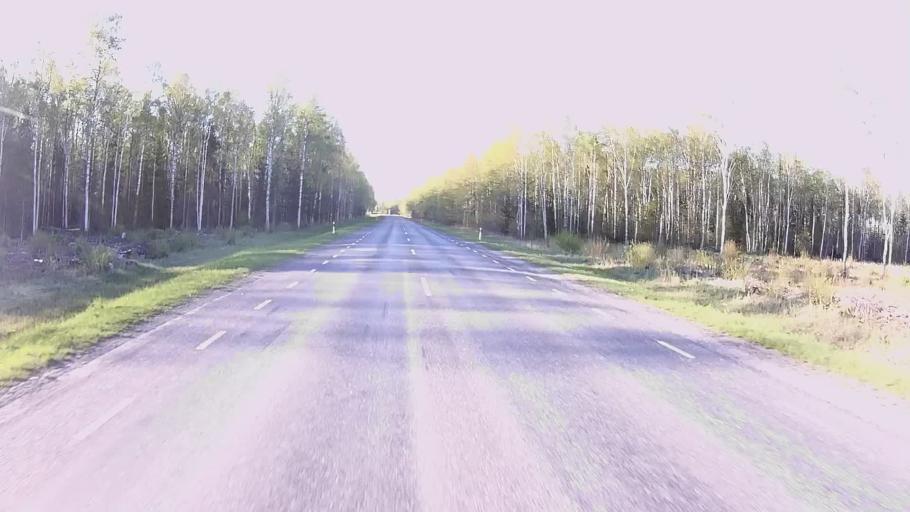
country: EE
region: Viljandimaa
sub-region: Vohma linn
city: Vohma
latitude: 58.5972
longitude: 25.5724
